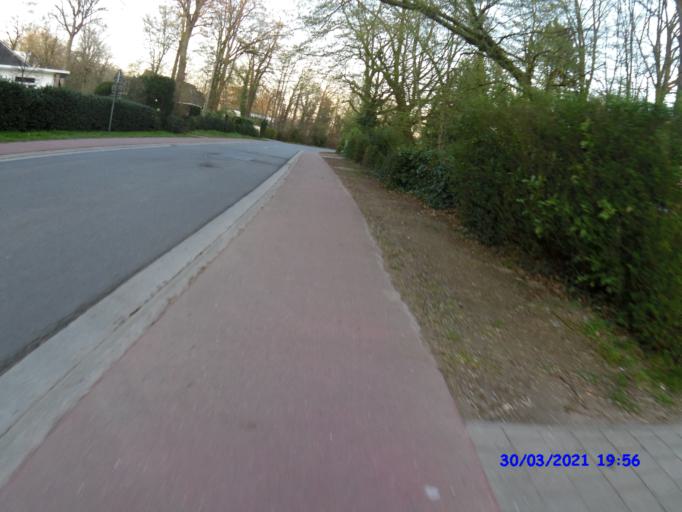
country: BE
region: Flanders
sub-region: Provincie Oost-Vlaanderen
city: Sint-Martens-Latem
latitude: 51.0286
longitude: 3.6697
